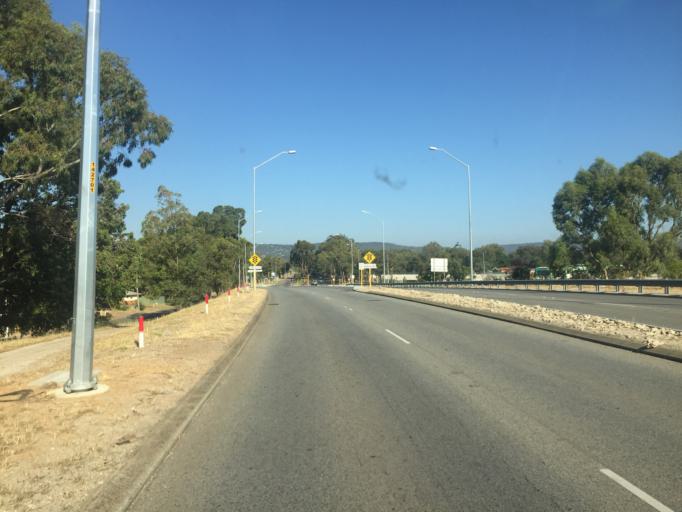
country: AU
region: Western Australia
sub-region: Canning
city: East Cannington
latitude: -32.0046
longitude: 115.9778
